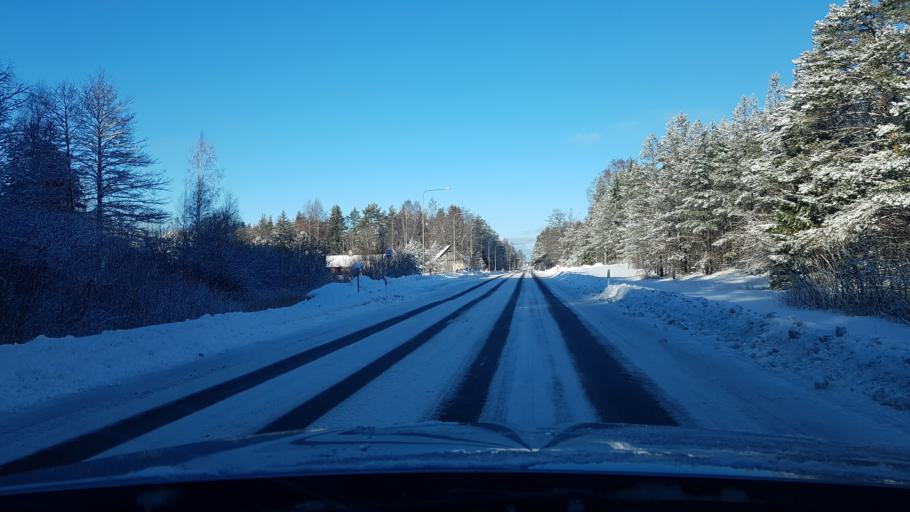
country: EE
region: Hiiumaa
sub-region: Kaerdla linn
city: Kardla
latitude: 58.9769
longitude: 22.7612
